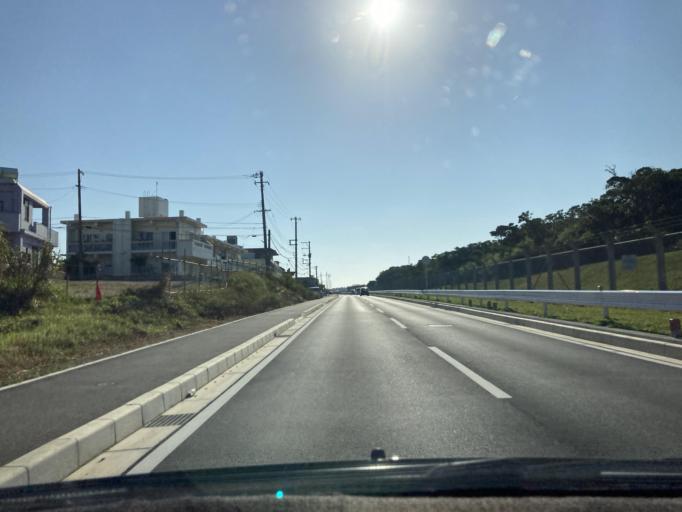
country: JP
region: Okinawa
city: Ginowan
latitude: 26.2720
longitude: 127.7660
